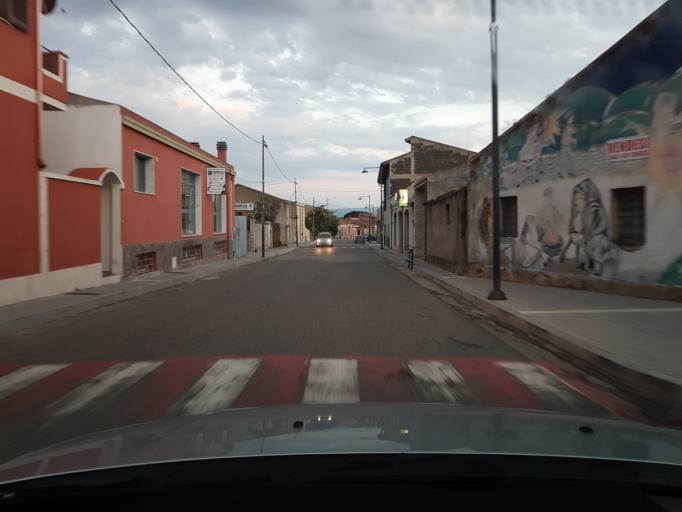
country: IT
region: Sardinia
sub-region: Provincia di Oristano
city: Tramatza
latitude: 40.0027
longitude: 8.6489
